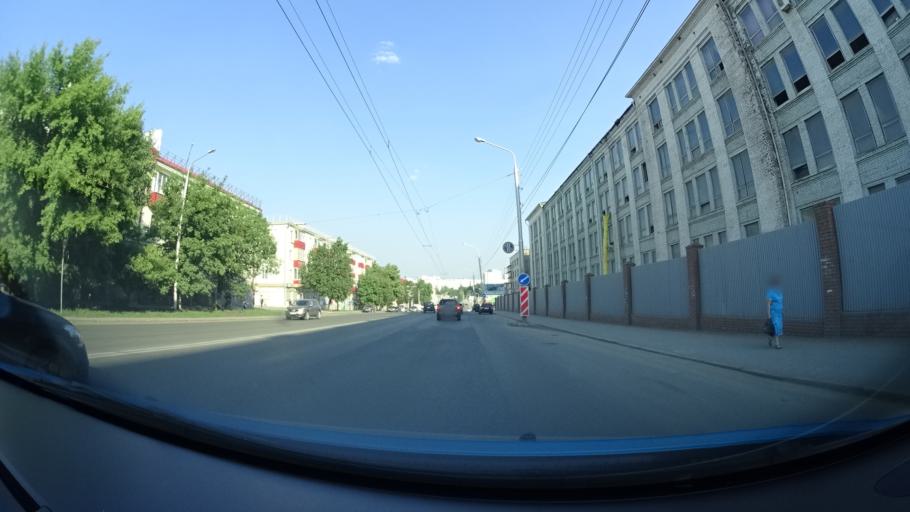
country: RU
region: Bashkortostan
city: Ufa
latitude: 54.7524
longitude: 56.0127
